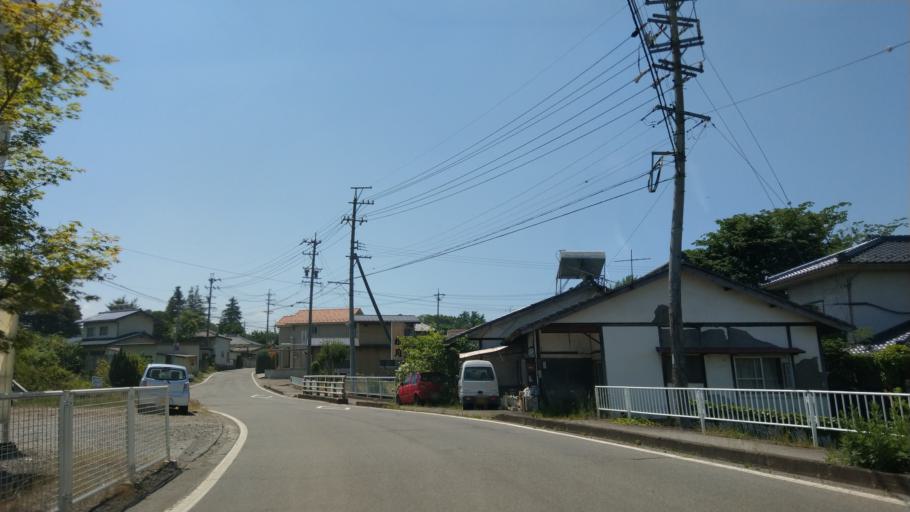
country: JP
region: Nagano
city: Komoro
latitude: 36.2852
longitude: 138.4425
